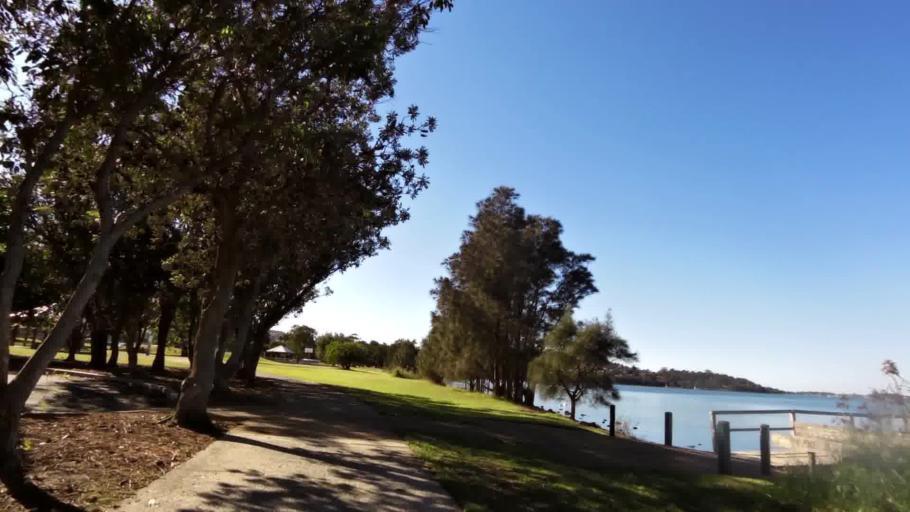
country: AU
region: New South Wales
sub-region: Wollongong
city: Berkeley
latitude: -34.4845
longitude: 150.8456
